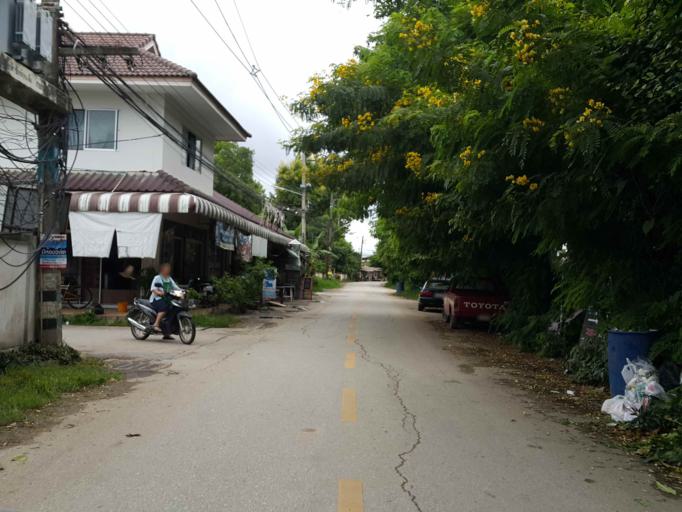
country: TH
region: Chiang Mai
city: Chiang Mai
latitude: 18.8138
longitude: 98.9976
